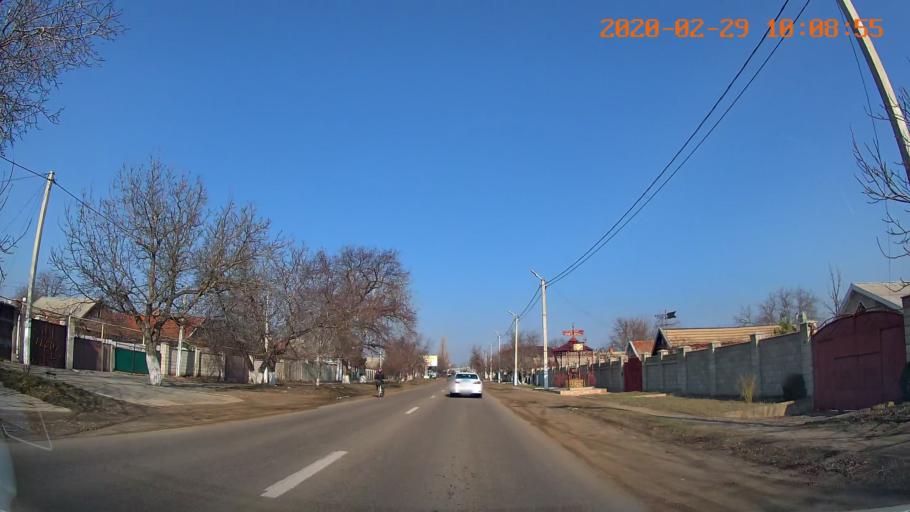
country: MD
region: Telenesti
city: Tiraspolul Nou
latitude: 46.8251
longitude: 29.6551
